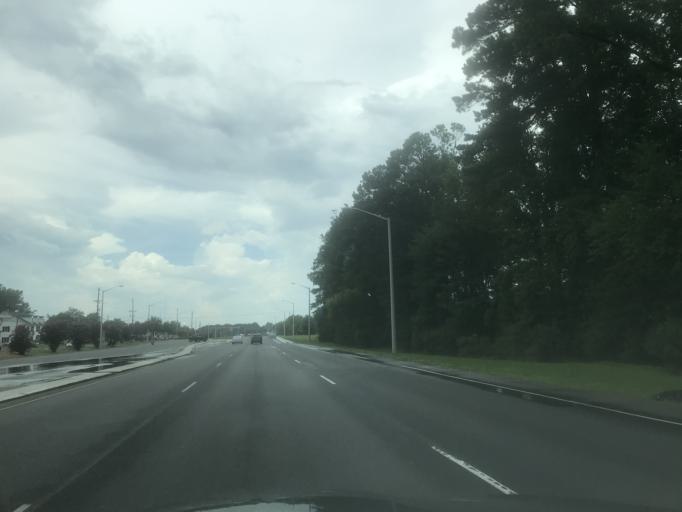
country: US
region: North Carolina
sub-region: Johnston County
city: Clayton
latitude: 35.6382
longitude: -78.4447
